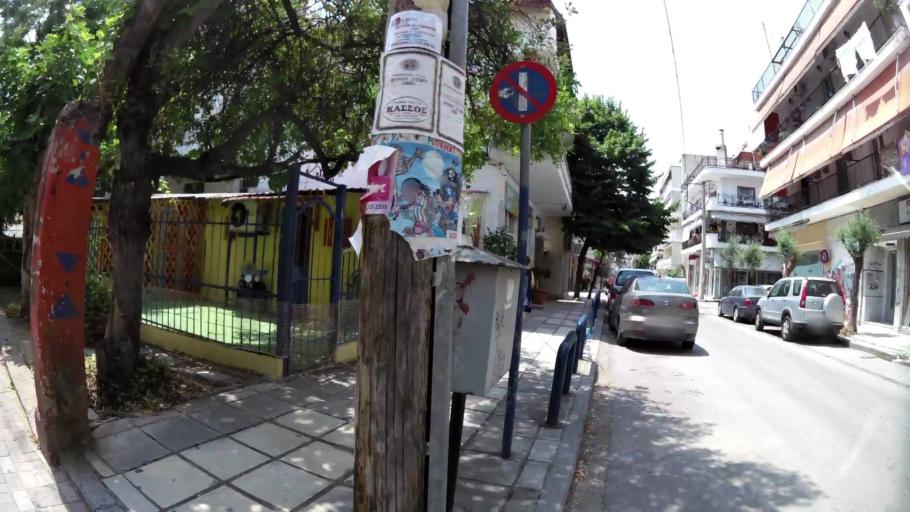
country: GR
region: Central Macedonia
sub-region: Nomos Thessalonikis
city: Evosmos
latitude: 40.6692
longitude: 22.9075
